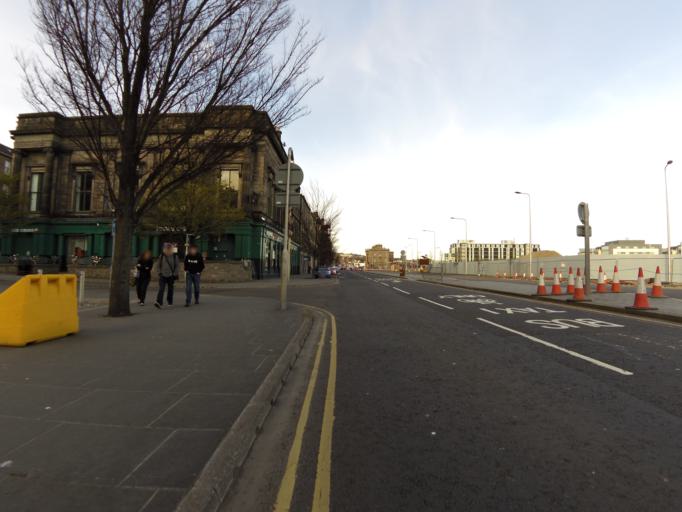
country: GB
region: Scotland
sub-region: Dundee City
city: Dundee
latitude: 56.4598
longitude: -2.9675
